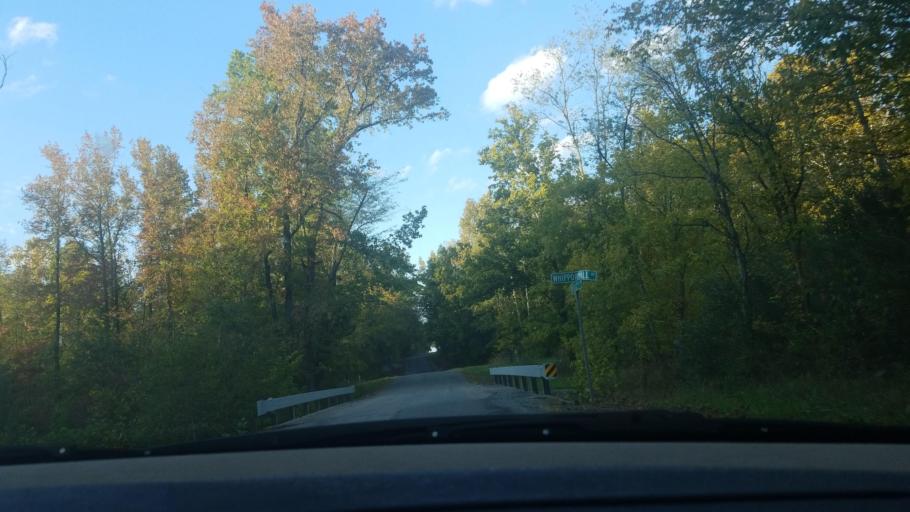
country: US
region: Illinois
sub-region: Saline County
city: Carrier Mills
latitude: 37.7866
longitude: -88.7117
